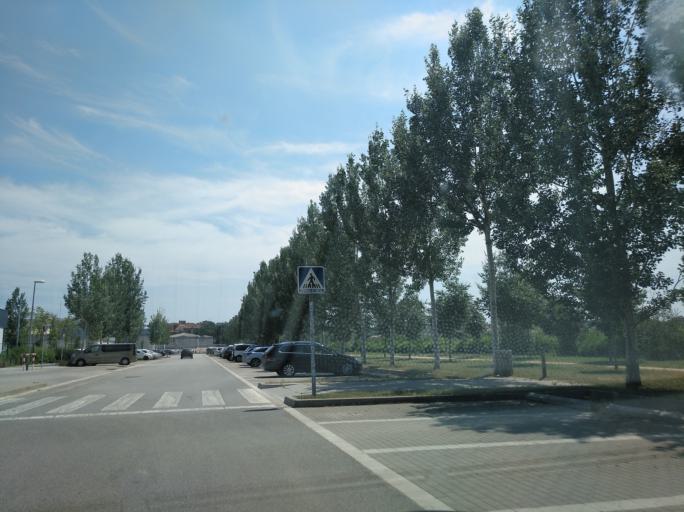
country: ES
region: Catalonia
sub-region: Provincia de Girona
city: Girona
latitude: 41.9830
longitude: 2.8091
